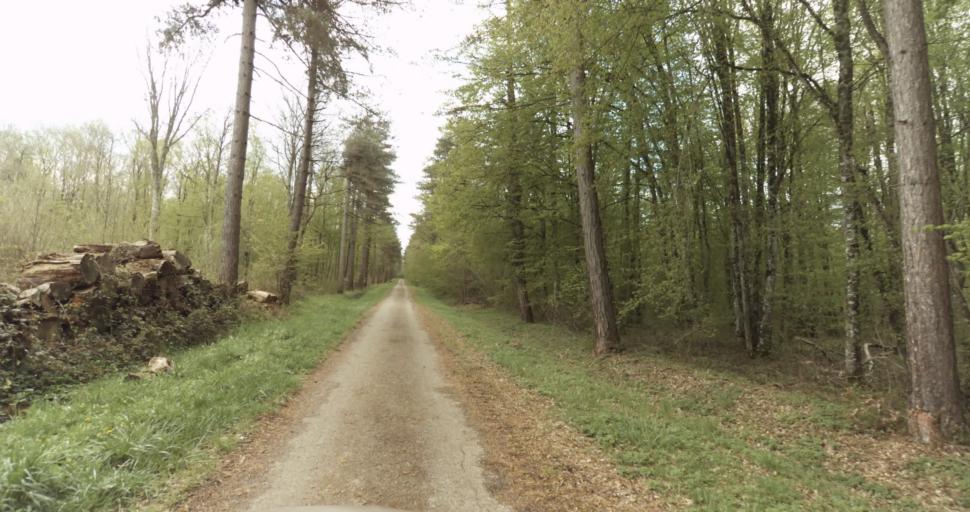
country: FR
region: Bourgogne
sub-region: Departement de la Cote-d'Or
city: Auxonne
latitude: 47.1595
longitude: 5.4228
